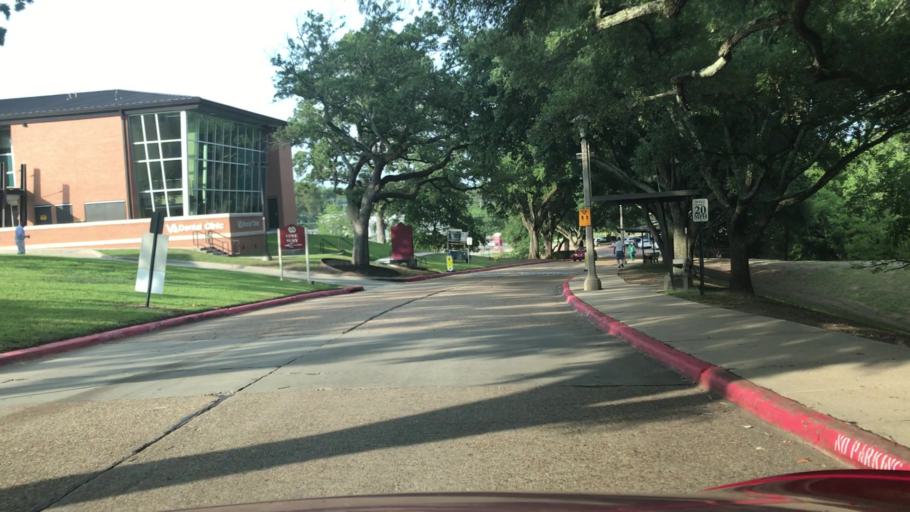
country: US
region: Louisiana
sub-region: Bossier Parish
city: Bossier City
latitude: 32.5018
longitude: -93.7211
